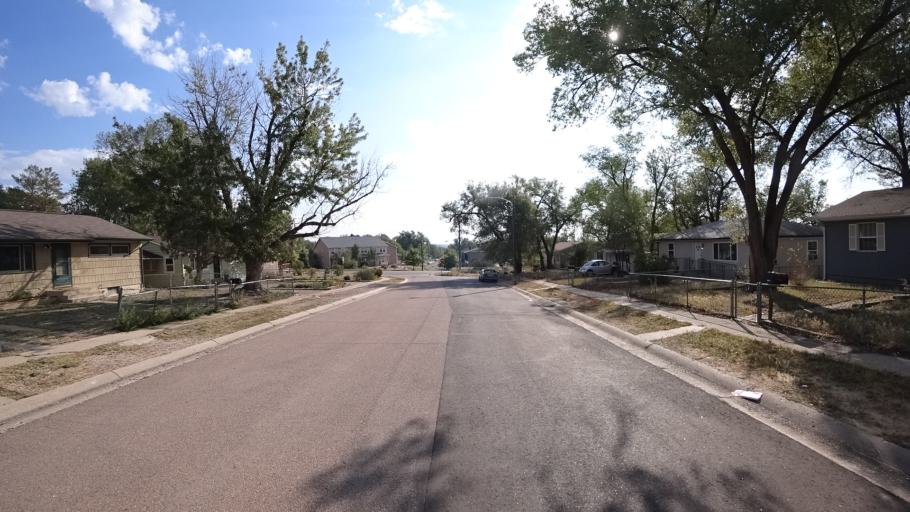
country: US
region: Colorado
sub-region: El Paso County
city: Colorado Springs
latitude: 38.8210
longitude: -104.7952
